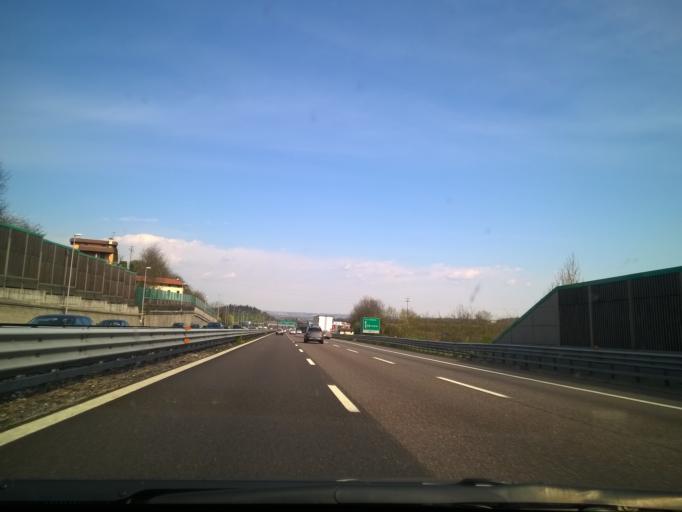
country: IT
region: Lombardy
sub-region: Provincia di Brescia
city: Lonato
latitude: 45.4509
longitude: 10.5075
